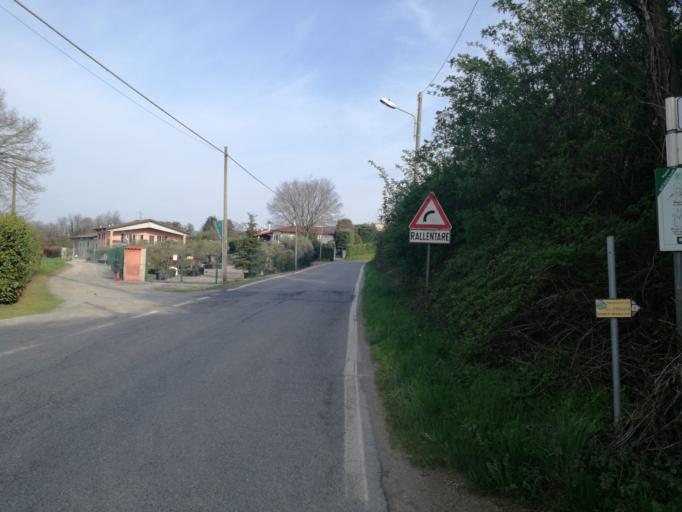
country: IT
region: Lombardy
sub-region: Provincia di Lecco
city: Paderno d'Adda
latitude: 45.6747
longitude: 9.4553
